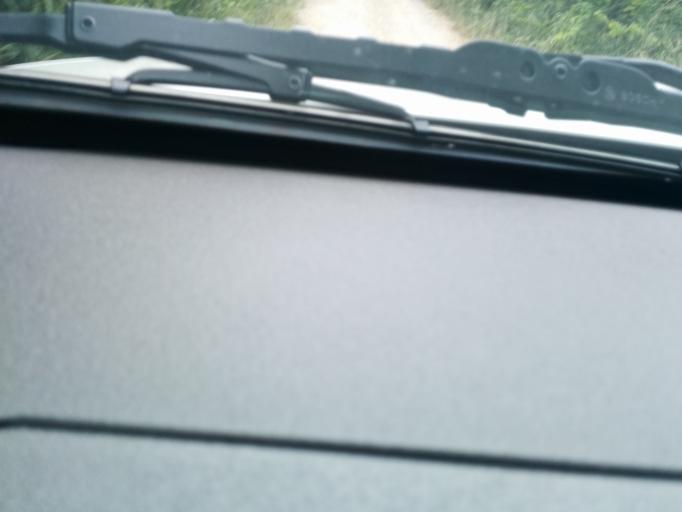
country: TH
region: Sara Buri
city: Muak Lek
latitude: 14.6140
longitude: 101.2087
